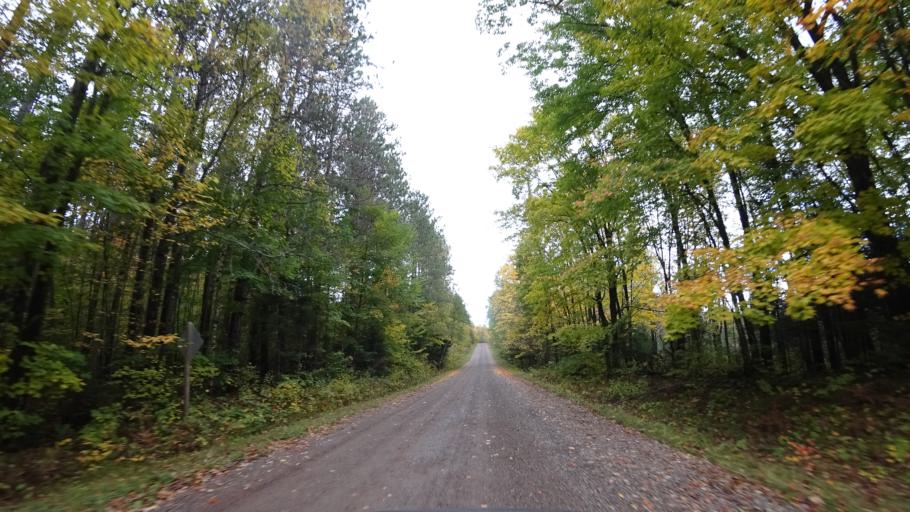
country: US
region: Wisconsin
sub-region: Sawyer County
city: Little Round Lake
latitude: 45.9631
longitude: -90.9804
